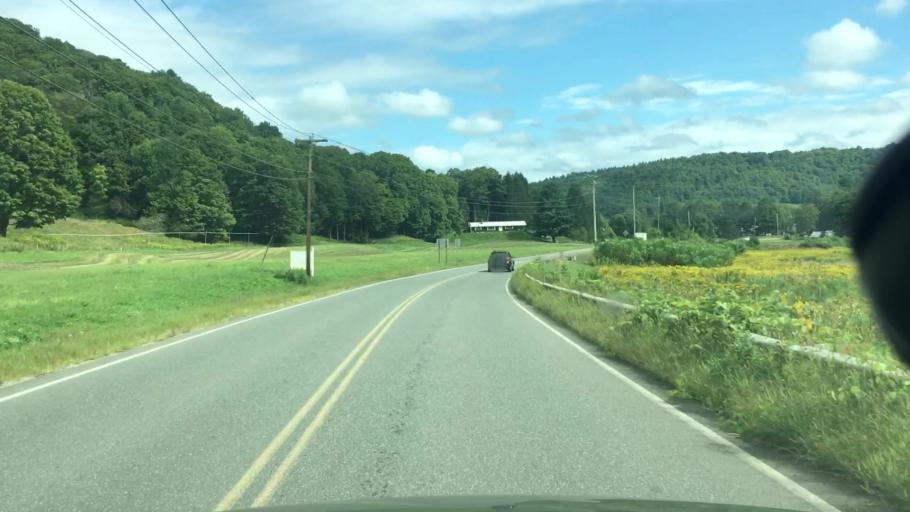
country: US
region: Massachusetts
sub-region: Franklin County
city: Colrain
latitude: 42.6775
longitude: -72.6954
